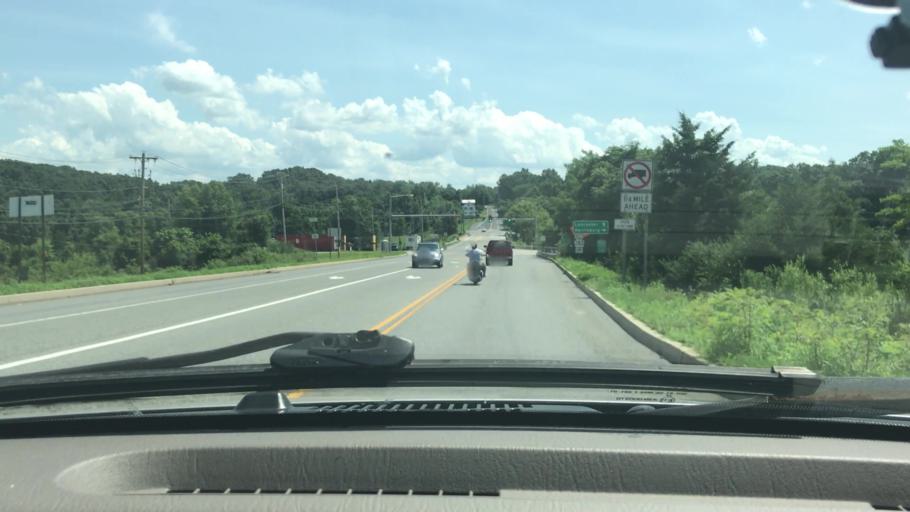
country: US
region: Pennsylvania
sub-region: Dauphin County
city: Middletown
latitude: 40.2295
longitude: -76.7379
